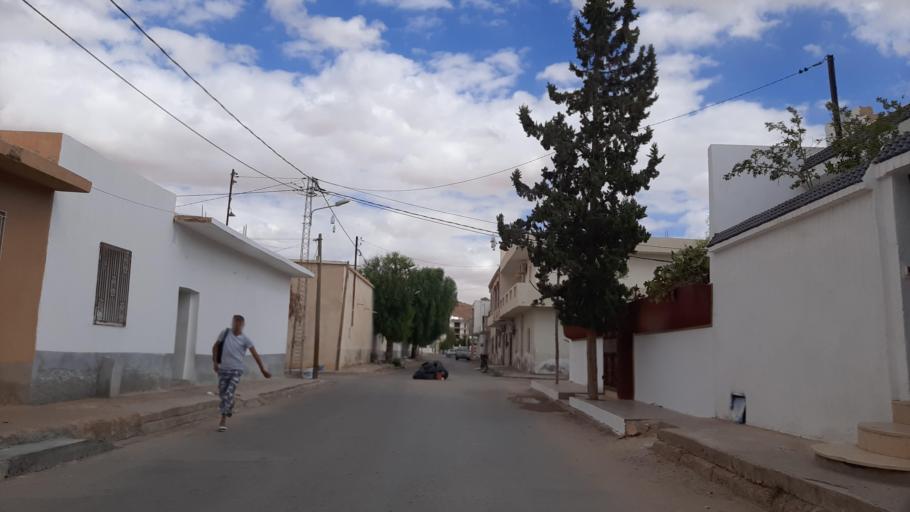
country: TN
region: Tataouine
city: Tataouine
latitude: 32.9342
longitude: 10.4498
